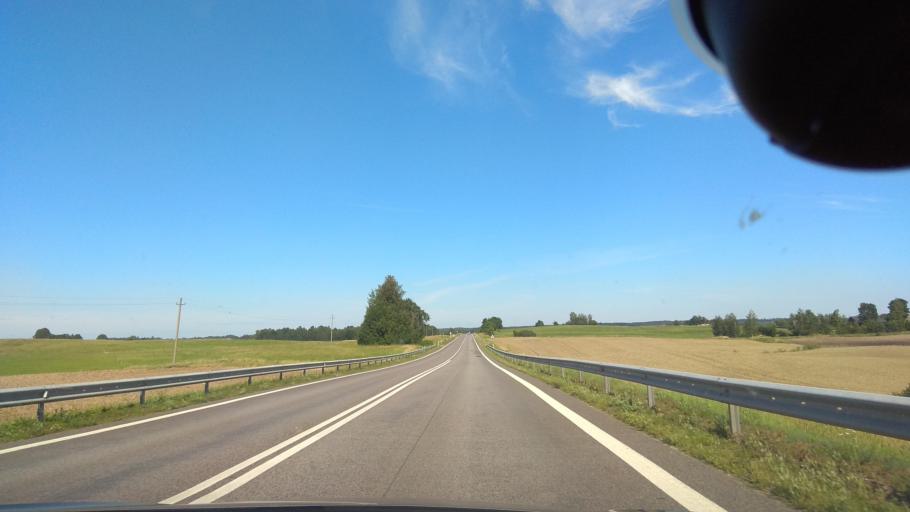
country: LT
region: Telsiu apskritis
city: Plunge
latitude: 55.9780
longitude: 22.0249
